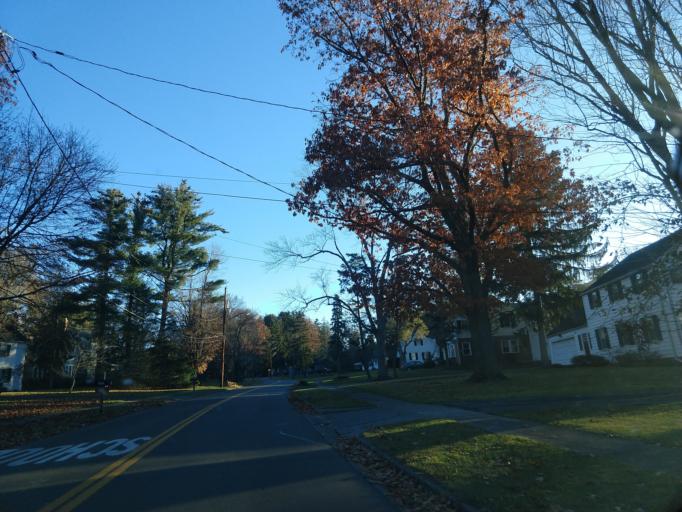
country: US
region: New York
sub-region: Tompkins County
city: Cayuga Heights
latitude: 42.4657
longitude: -76.4860
